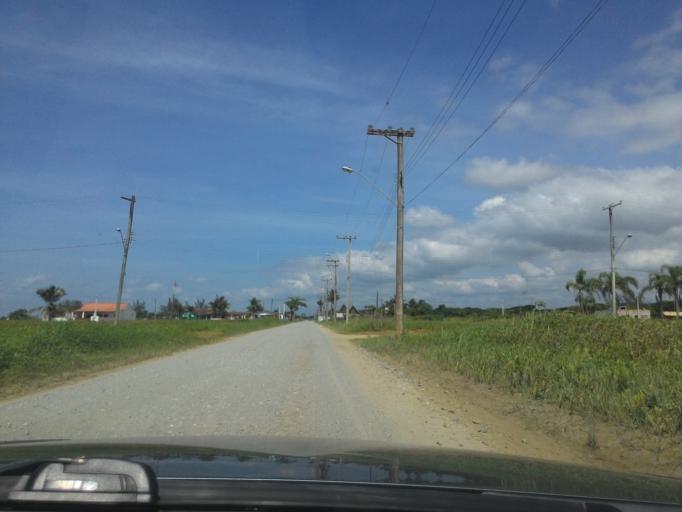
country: BR
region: Sao Paulo
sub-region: Iguape
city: Iguape
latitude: -24.8469
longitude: -47.6940
